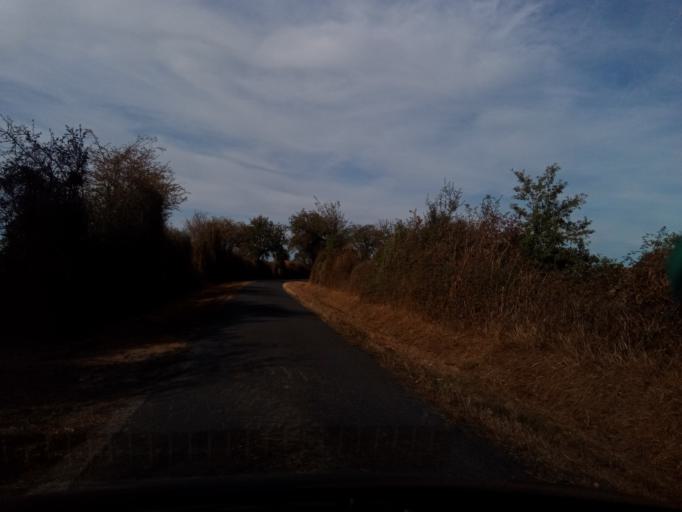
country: FR
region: Poitou-Charentes
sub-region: Departement de la Vienne
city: Saulge
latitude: 46.4036
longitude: 0.8691
